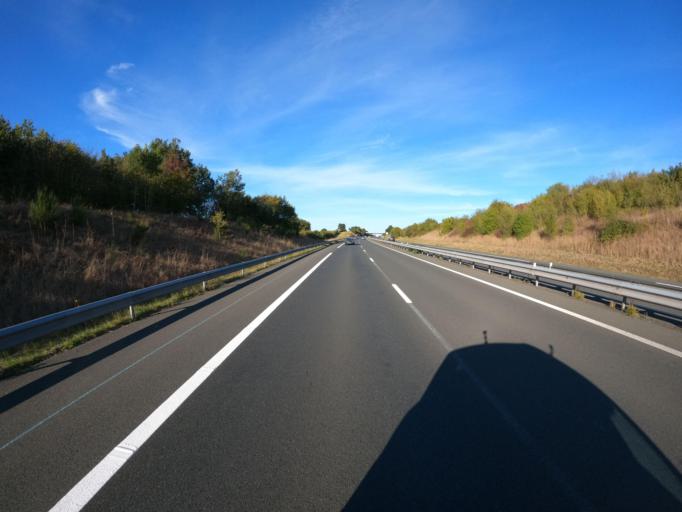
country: FR
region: Pays de la Loire
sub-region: Departement de Maine-et-Loire
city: Chemille-Melay
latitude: 47.2281
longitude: -0.7552
